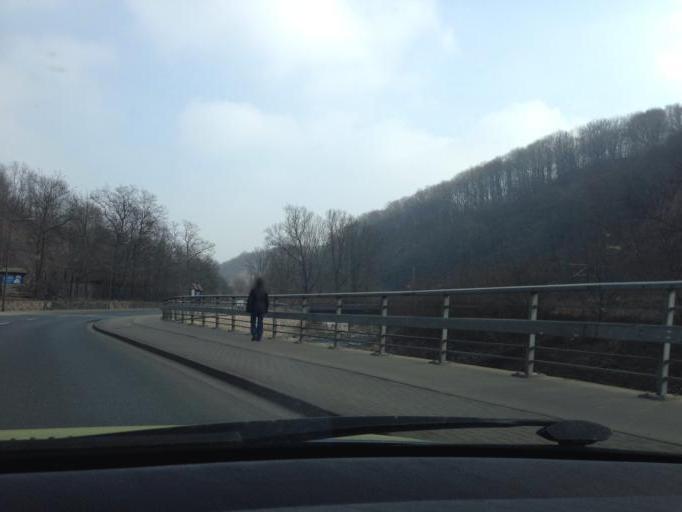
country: DE
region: Saxony
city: Bannewitz
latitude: 51.0229
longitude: 13.6876
